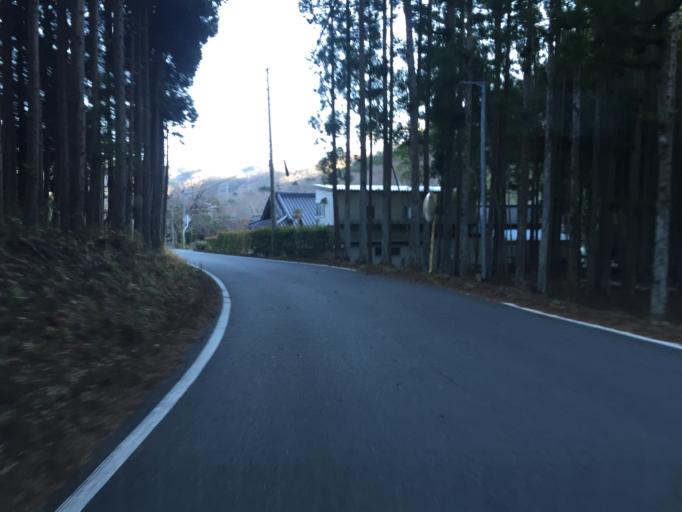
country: JP
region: Fukushima
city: Iwaki
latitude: 37.1841
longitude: 140.8169
